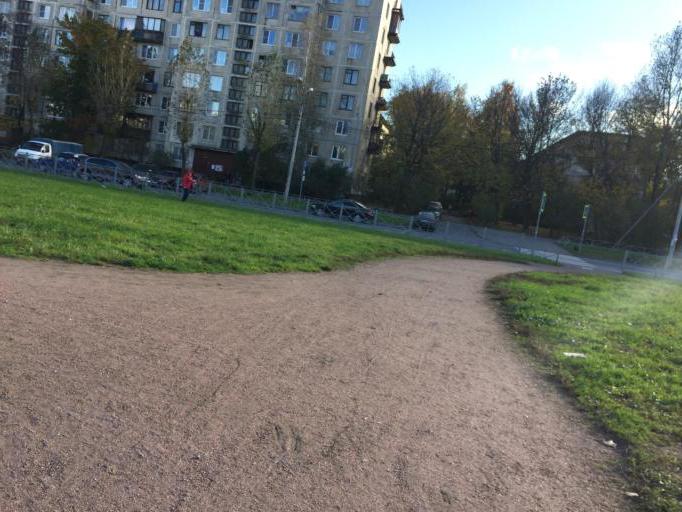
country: RU
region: St.-Petersburg
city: Obukhovo
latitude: 59.8956
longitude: 30.4675
